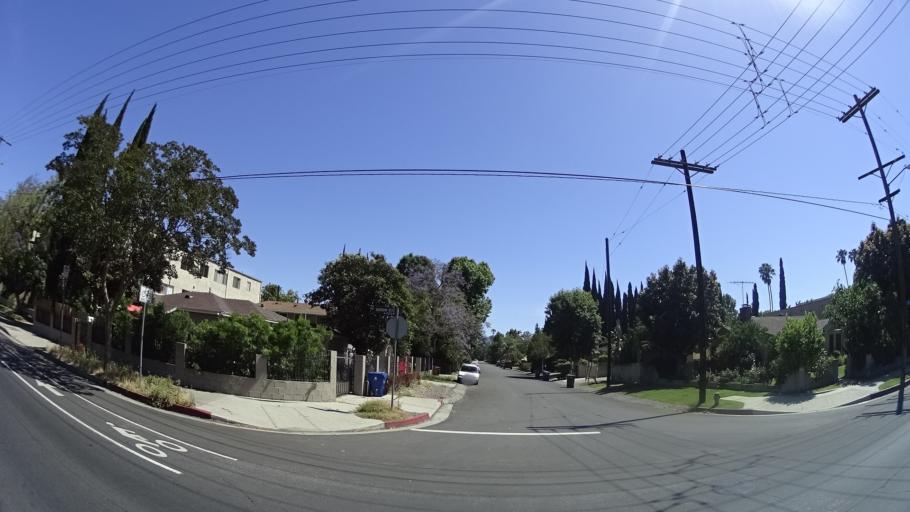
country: US
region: California
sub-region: Los Angeles County
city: Van Nuys
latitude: 34.1721
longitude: -118.4282
